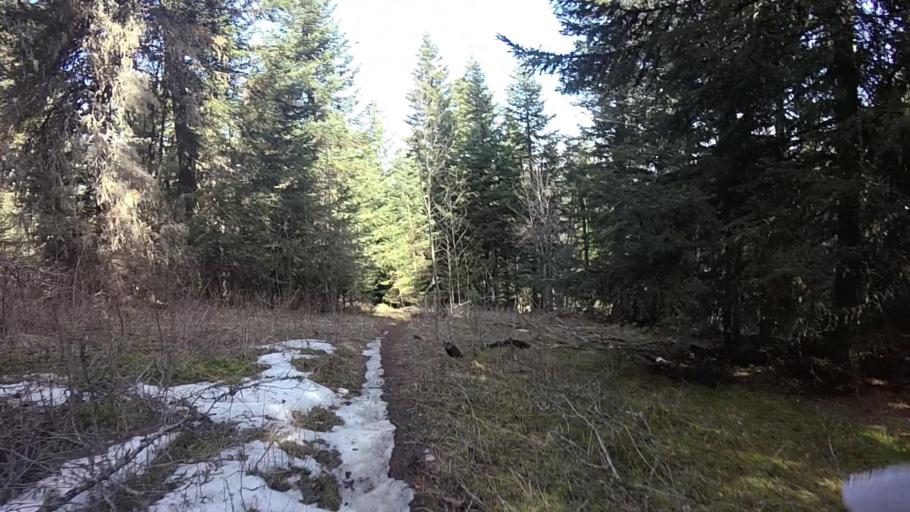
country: FR
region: Provence-Alpes-Cote d'Azur
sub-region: Departement des Alpes-de-Haute-Provence
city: Seyne-les-Alpes
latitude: 44.3424
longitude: 6.3028
